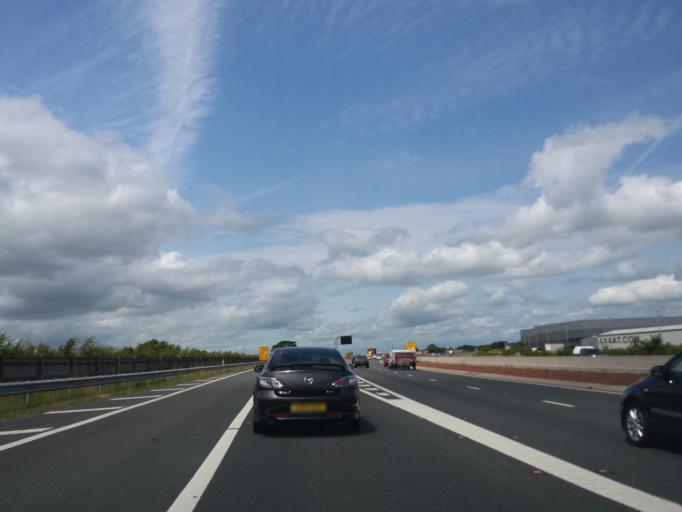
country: GB
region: England
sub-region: North Yorkshire
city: Bedale
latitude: 54.3041
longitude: -1.5702
